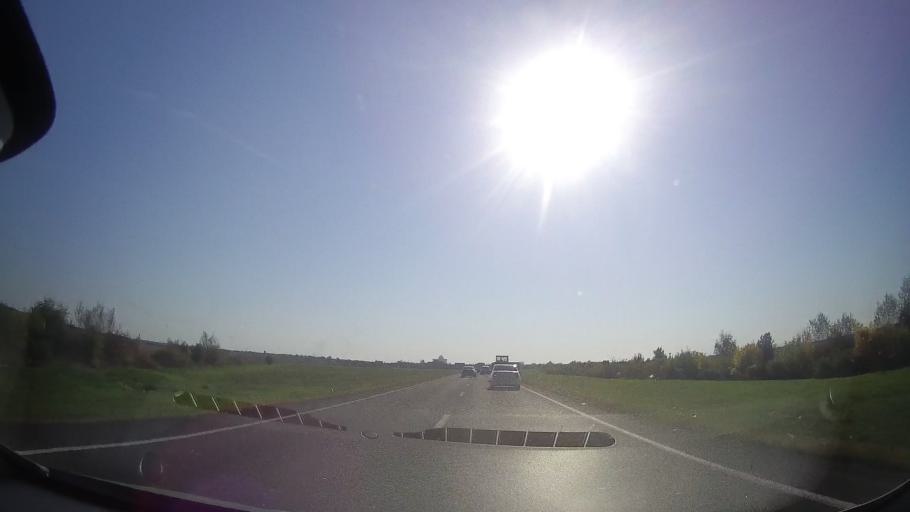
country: RO
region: Timis
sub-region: Comuna Topolovatu Mare
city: Topolovatu Mare
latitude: 45.7811
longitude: 21.6053
